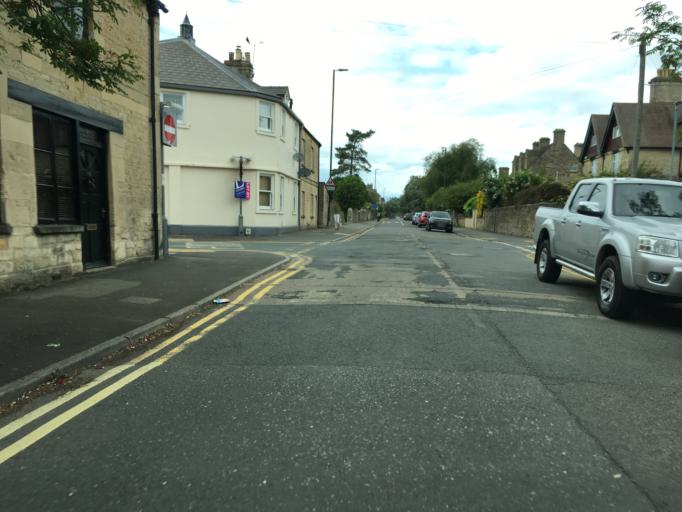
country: GB
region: England
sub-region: Gloucestershire
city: Cirencester
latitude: 51.7108
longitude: -1.9598
